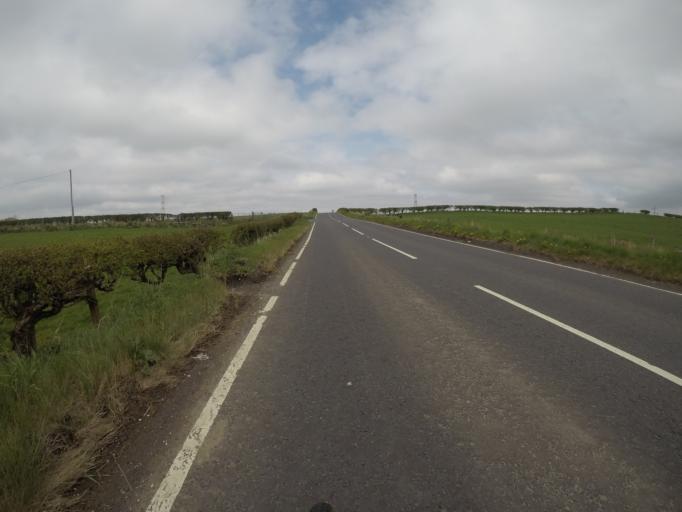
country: GB
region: Scotland
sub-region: East Renfrewshire
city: Barrhead
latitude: 55.7636
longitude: -4.3764
